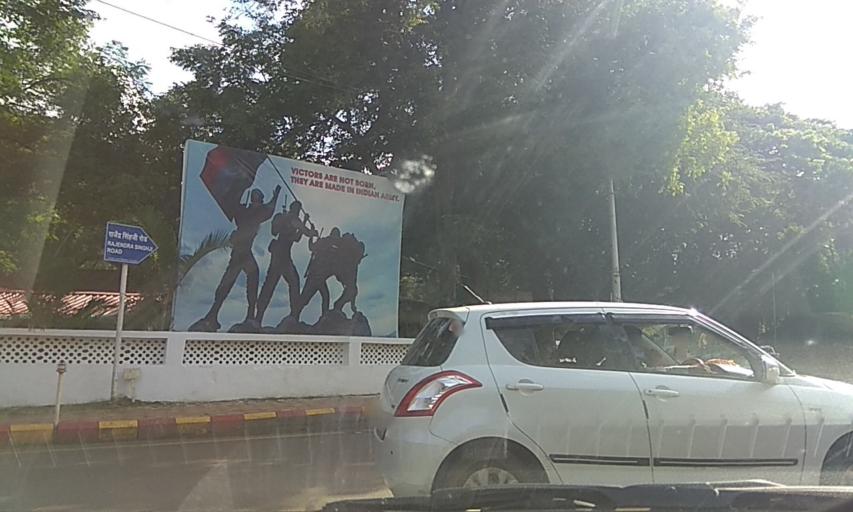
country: IN
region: Maharashtra
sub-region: Pune Division
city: Pune
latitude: 18.5237
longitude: 73.8830
